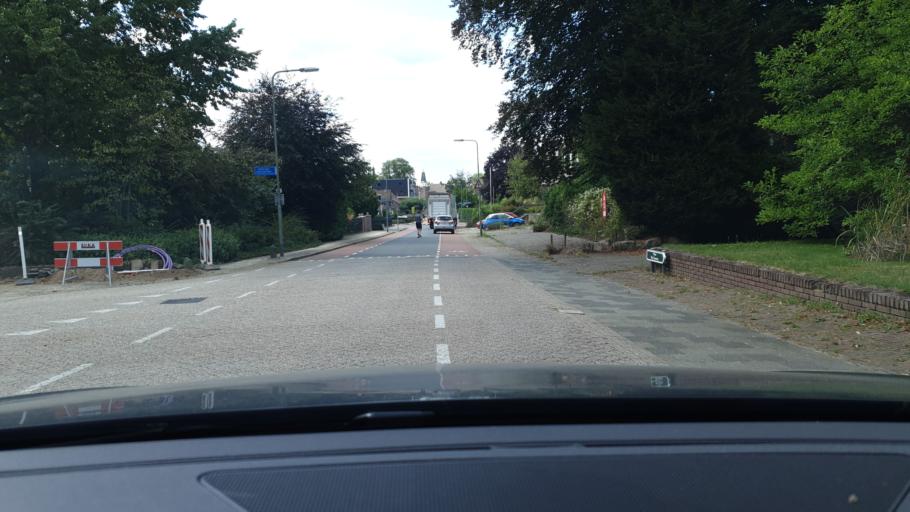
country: NL
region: North Brabant
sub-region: Gemeente Cuijk
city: Cuijk
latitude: 51.7533
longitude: 5.8854
